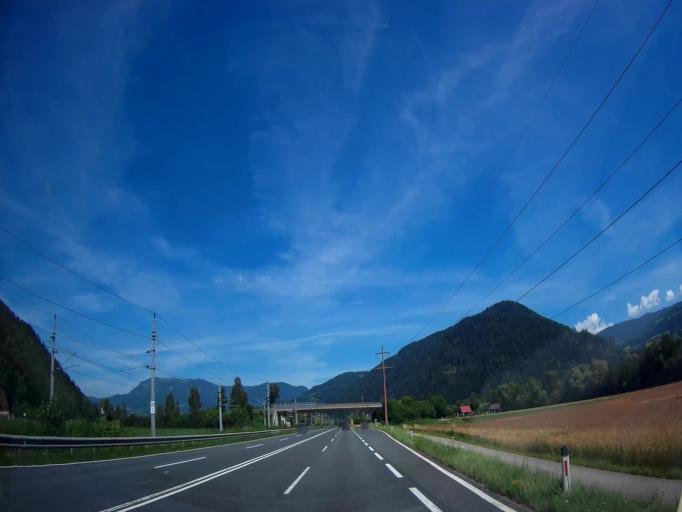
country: AT
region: Carinthia
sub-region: Politischer Bezirk Sankt Veit an der Glan
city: Micheldorf
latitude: 46.9378
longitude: 14.4251
